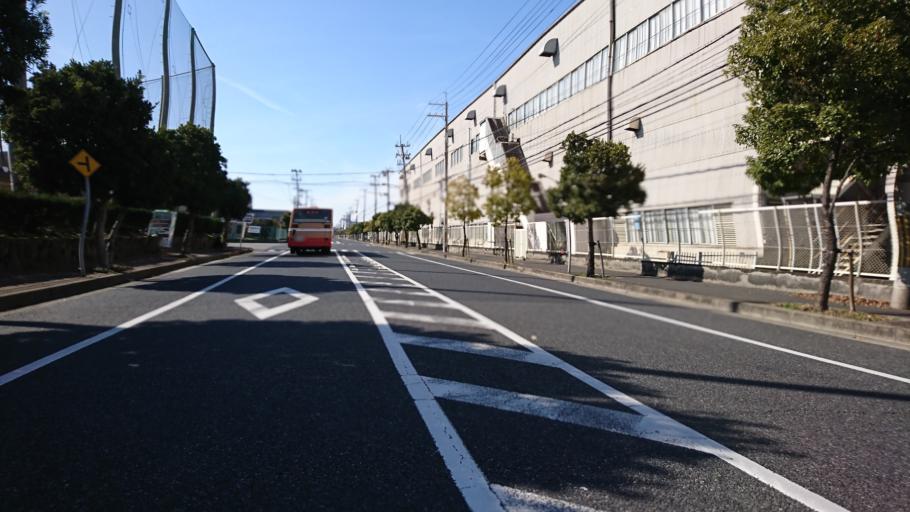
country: JP
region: Hyogo
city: Kakogawacho-honmachi
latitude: 34.7025
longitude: 134.8511
